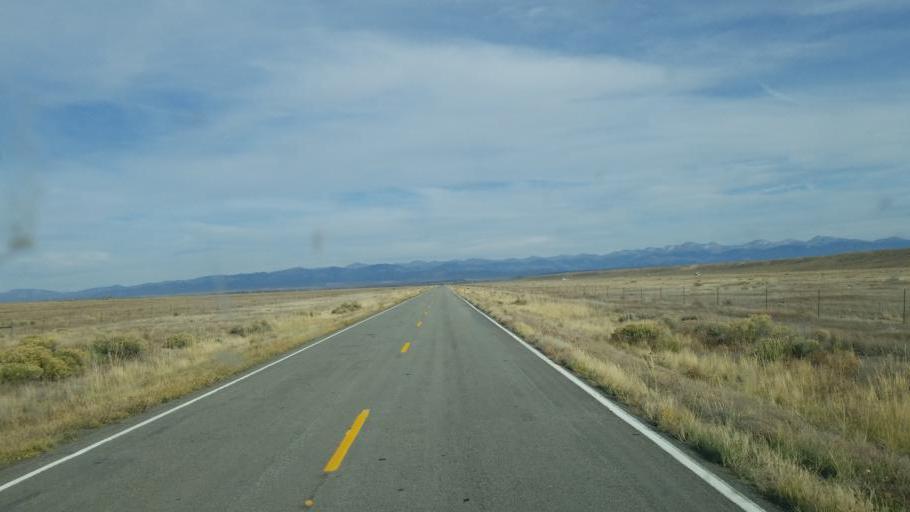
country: US
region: Colorado
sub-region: Costilla County
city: San Luis
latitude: 37.1816
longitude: -105.6171
